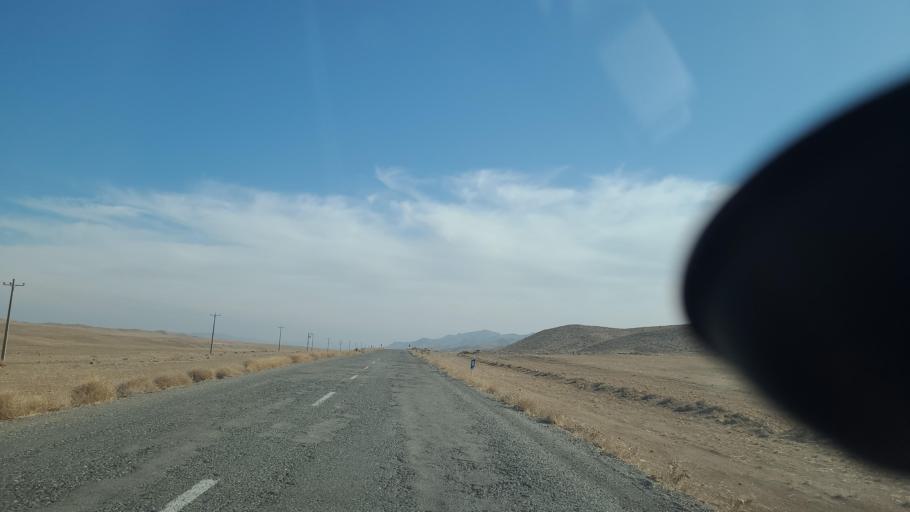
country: IR
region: Razavi Khorasan
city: Fariman
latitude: 35.5904
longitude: 59.6129
